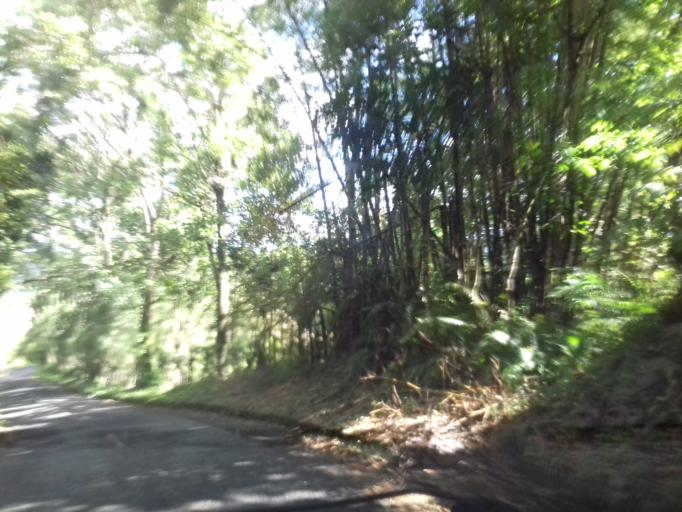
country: MQ
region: Martinique
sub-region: Martinique
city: Saint-Joseph
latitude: 14.6971
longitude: -61.0360
